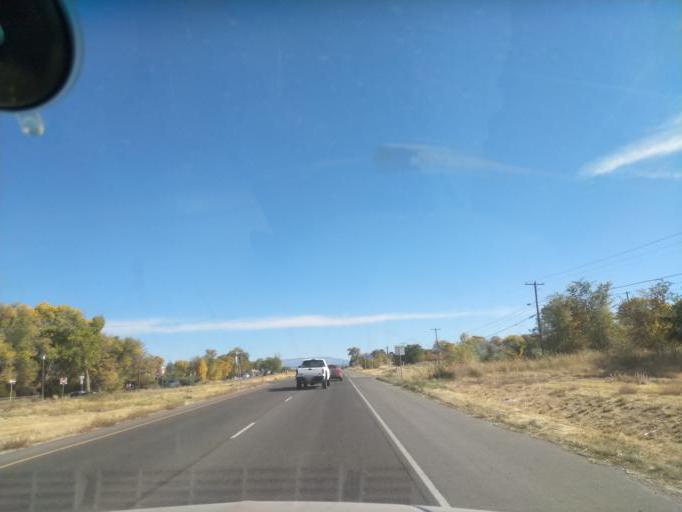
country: US
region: Colorado
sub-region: Mesa County
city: Orchard Mesa
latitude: 39.0320
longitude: -108.5207
